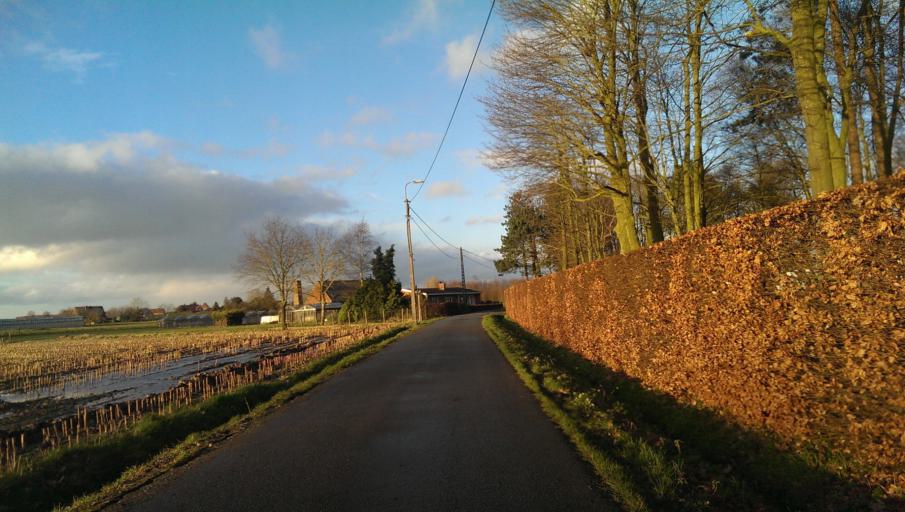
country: BE
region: Flanders
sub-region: Provincie West-Vlaanderen
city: Hooglede
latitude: 50.9374
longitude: 3.0737
